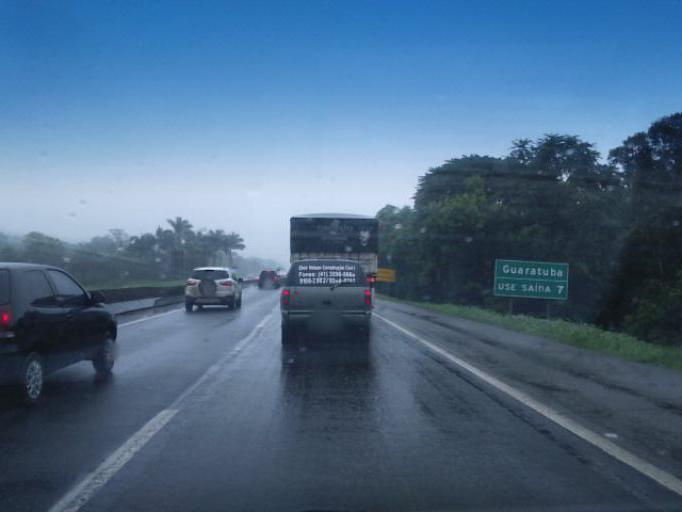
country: BR
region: Santa Catarina
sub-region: Joinville
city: Joinville
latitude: -26.0407
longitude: -48.8596
